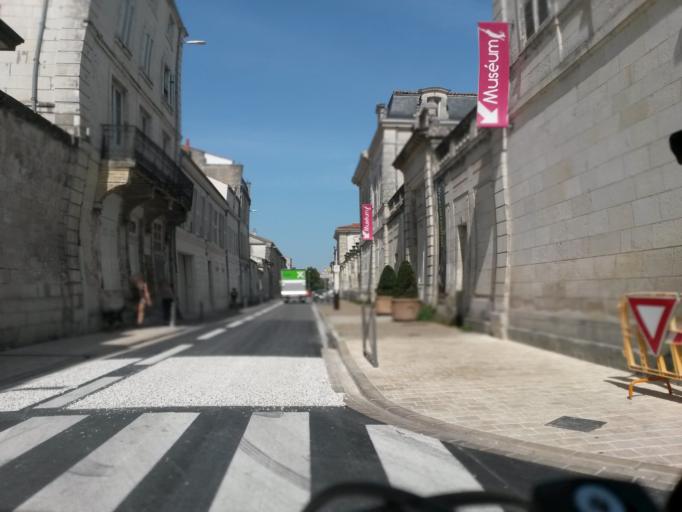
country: FR
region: Poitou-Charentes
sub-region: Departement de la Charente-Maritime
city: La Rochelle
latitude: 46.1647
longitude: -1.1516
